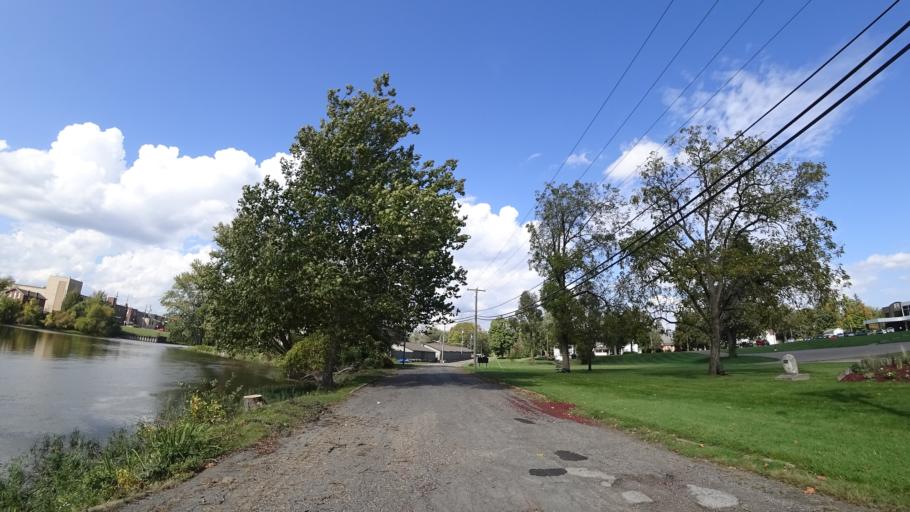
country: US
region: Michigan
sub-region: Saint Joseph County
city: Three Rivers
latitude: 41.9431
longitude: -85.6297
